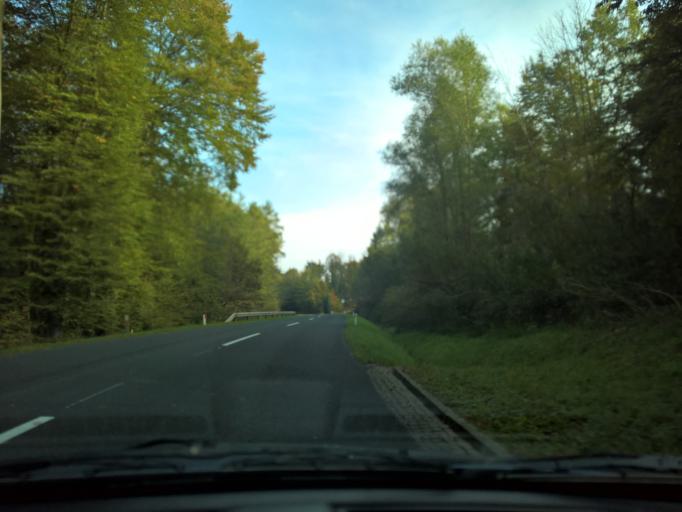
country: AT
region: Styria
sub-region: Politischer Bezirk Deutschlandsberg
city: Unterbergla
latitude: 46.7949
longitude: 15.3363
